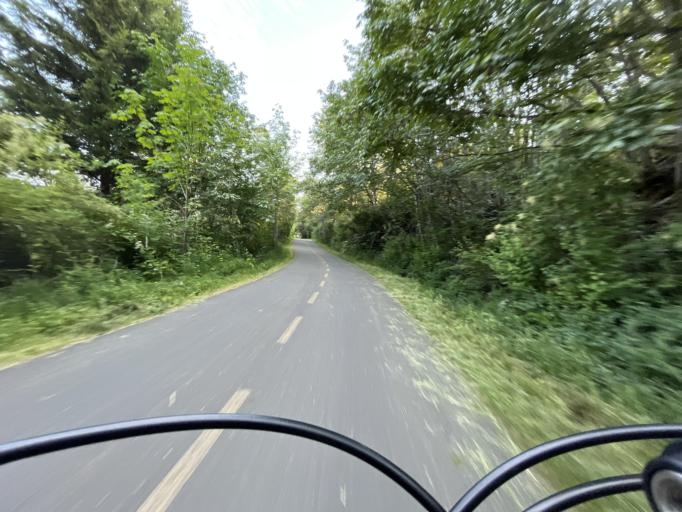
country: CA
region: British Columbia
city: Colwood
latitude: 48.4552
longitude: -123.4690
